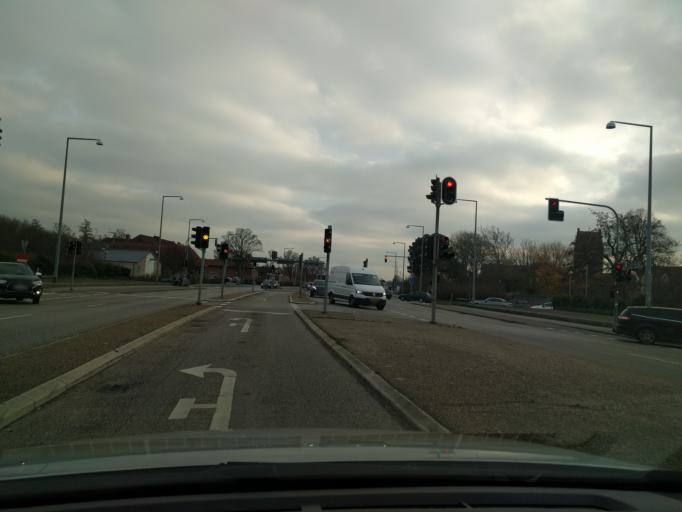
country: DK
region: Capital Region
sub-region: Tarnby Kommune
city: Tarnby
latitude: 55.6305
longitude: 12.5993
